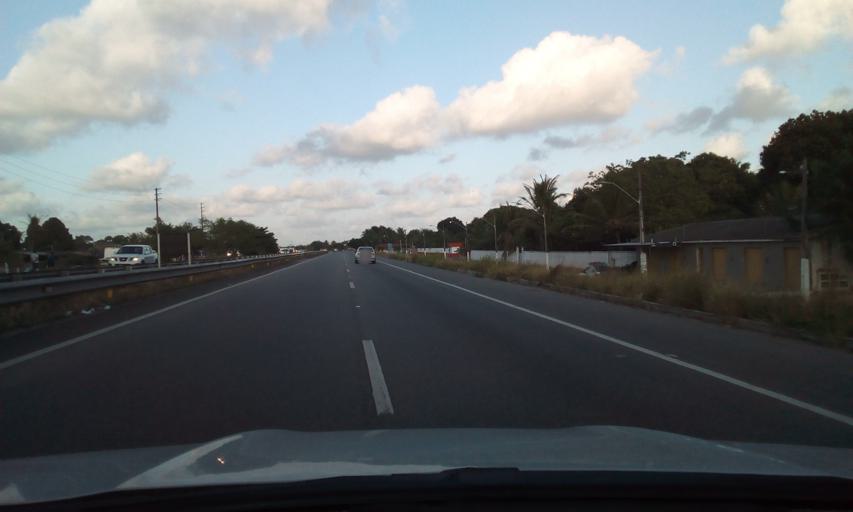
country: BR
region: Paraiba
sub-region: Bayeux
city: Bayeux
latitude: -7.1316
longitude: -34.9570
